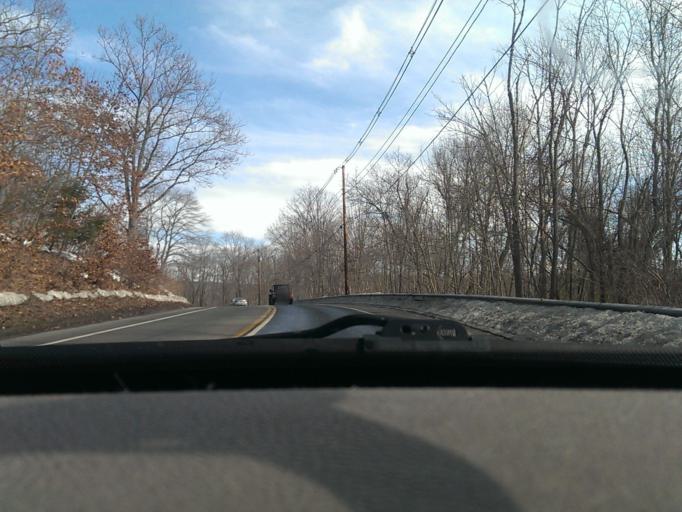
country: US
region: Massachusetts
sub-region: Hampden County
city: Three Rivers
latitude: 42.1523
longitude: -72.3823
